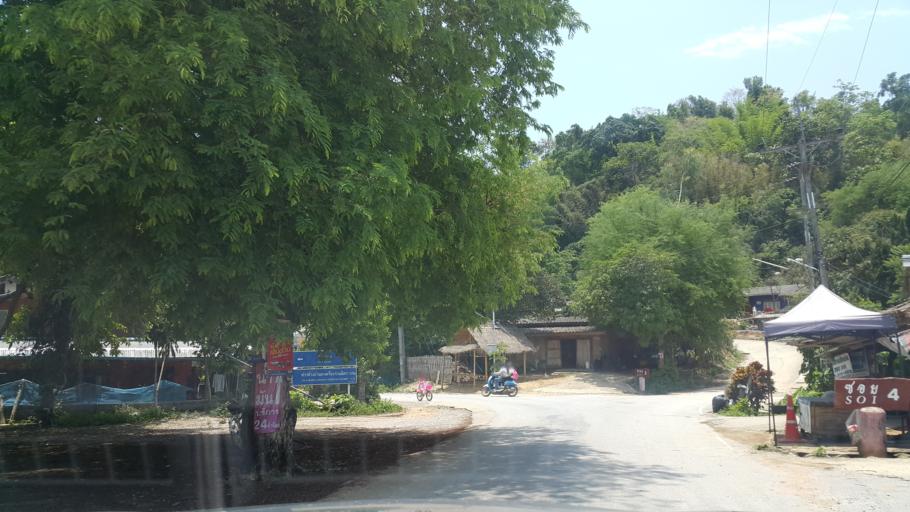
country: TH
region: Chiang Rai
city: Chiang Rai
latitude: 19.9821
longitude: 99.7316
